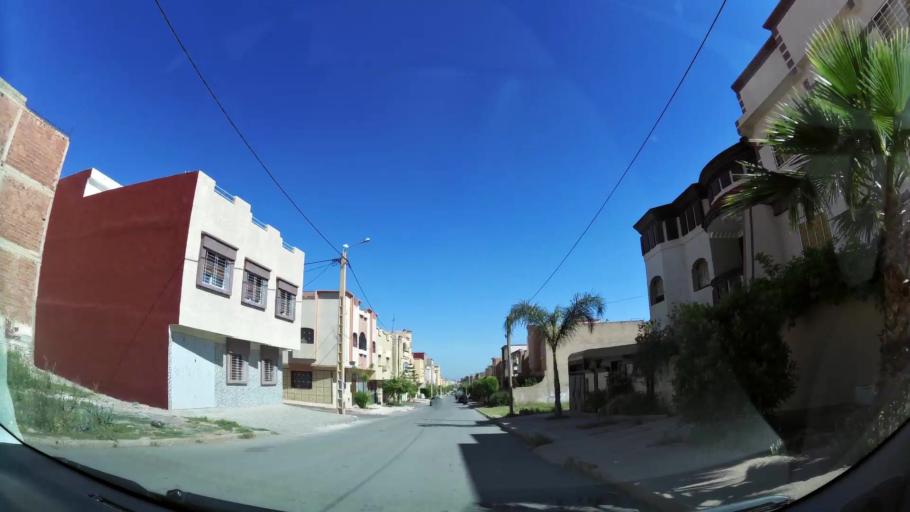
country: MA
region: Oriental
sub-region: Oujda-Angad
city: Oujda
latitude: 34.6556
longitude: -1.8871
